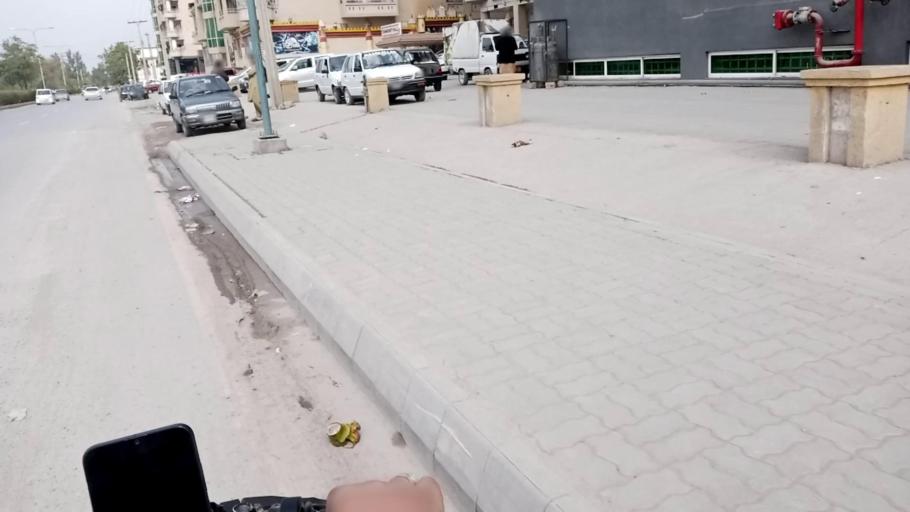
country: PK
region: Khyber Pakhtunkhwa
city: Peshawar
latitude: 33.9697
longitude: 71.4368
